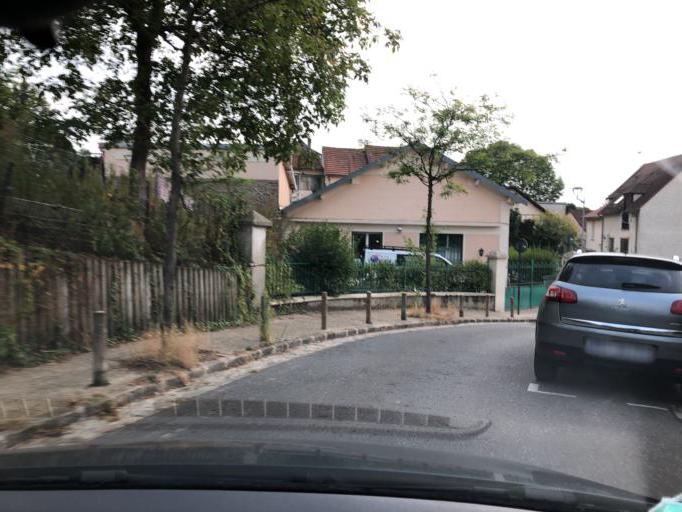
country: FR
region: Ile-de-France
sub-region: Departement des Hauts-de-Seine
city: Ville-d'Avray
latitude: 48.8154
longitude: 2.1973
